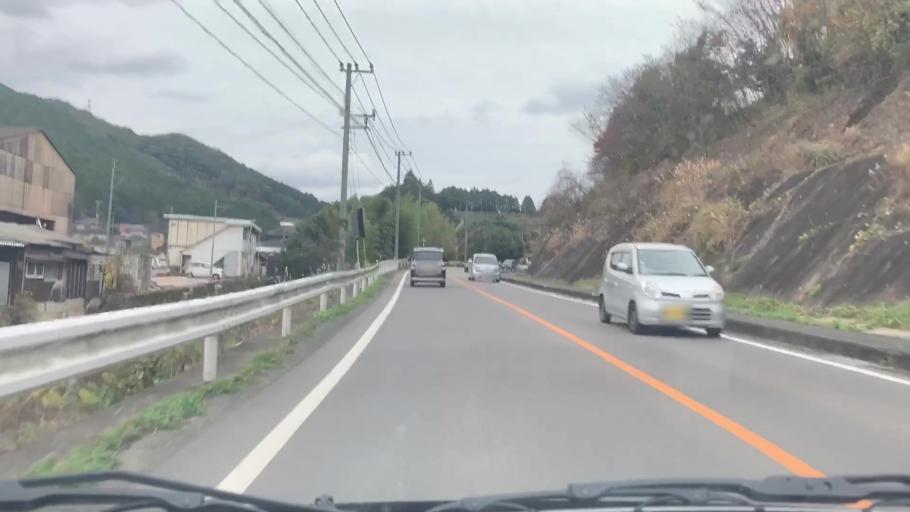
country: JP
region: Saga Prefecture
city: Ureshinomachi-shimojuku
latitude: 33.0975
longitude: 130.0020
